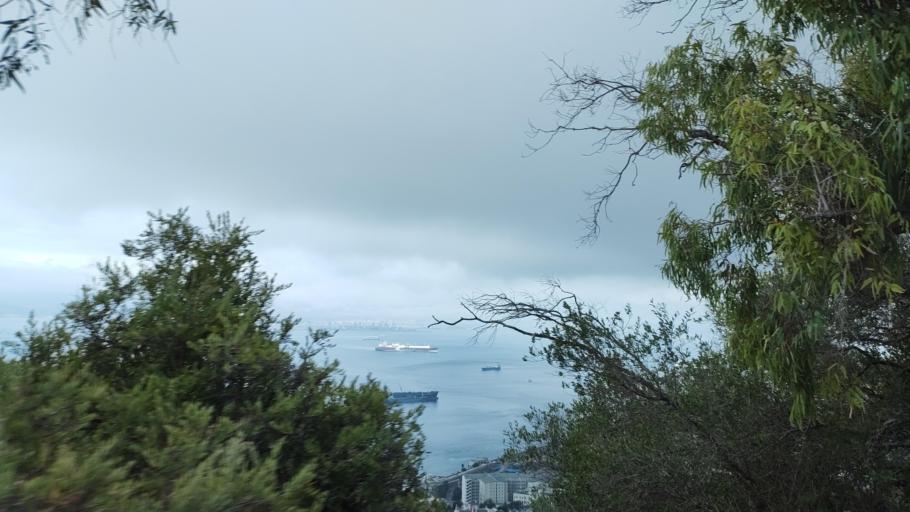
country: GI
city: Gibraltar
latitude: 36.1228
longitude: -5.3463
